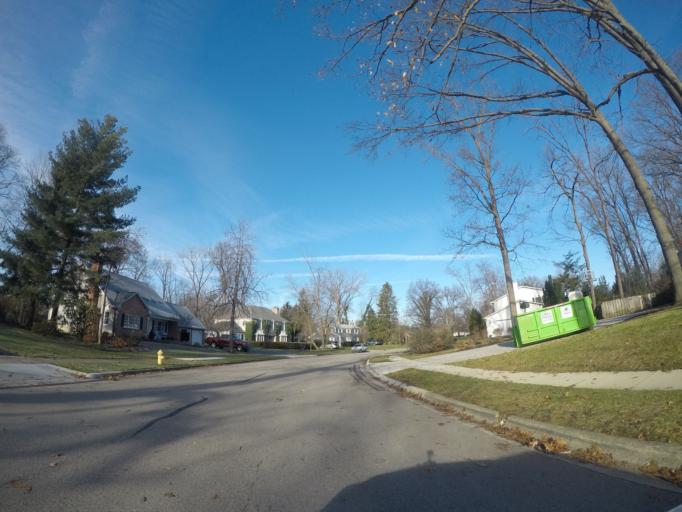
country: US
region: Ohio
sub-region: Franklin County
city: Upper Arlington
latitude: 40.0429
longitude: -83.0755
